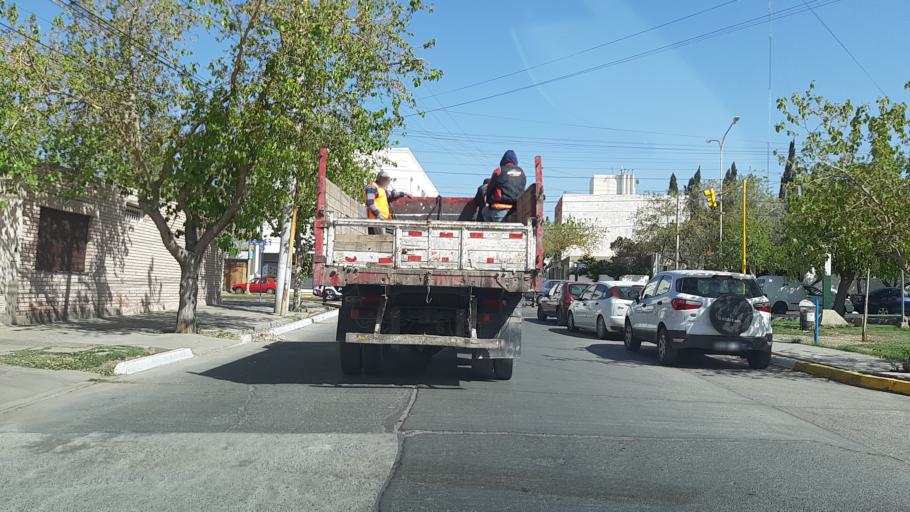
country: AR
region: San Juan
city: San Juan
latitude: -31.5311
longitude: -68.5316
